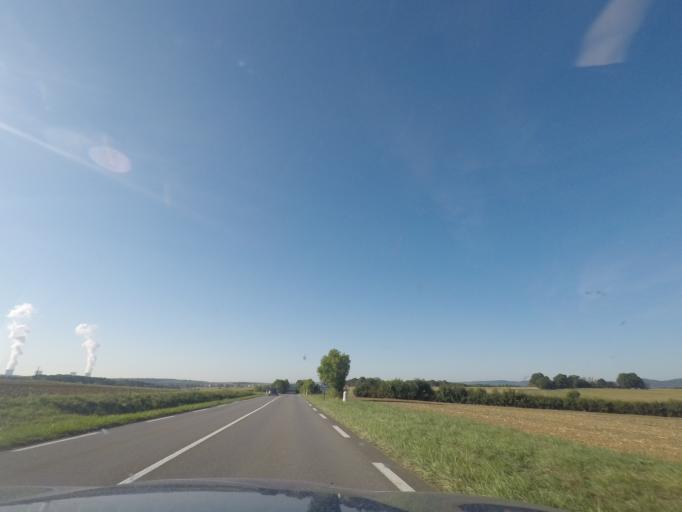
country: LU
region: Luxembourg
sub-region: Canton d'Esch-sur-Alzette
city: Frisange
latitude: 49.4780
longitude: 6.1886
